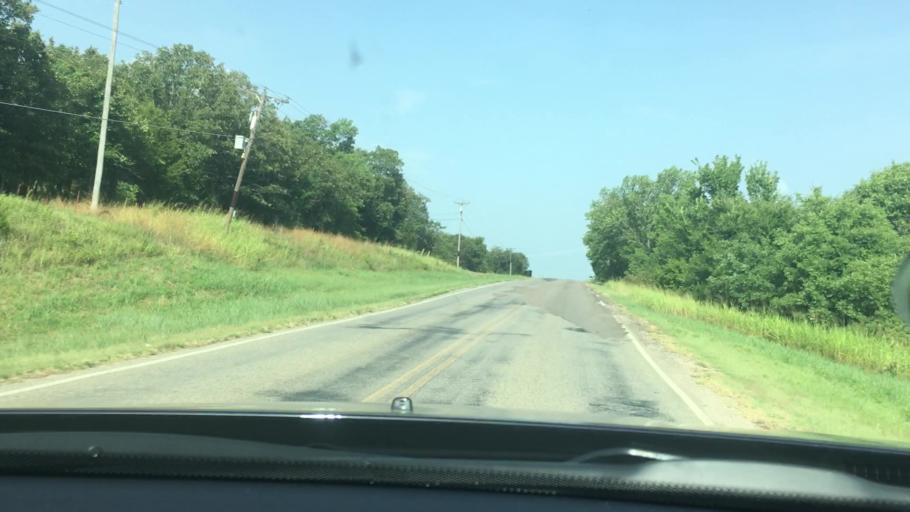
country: US
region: Oklahoma
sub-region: Pontotoc County
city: Byng
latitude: 34.8649
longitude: -96.6093
